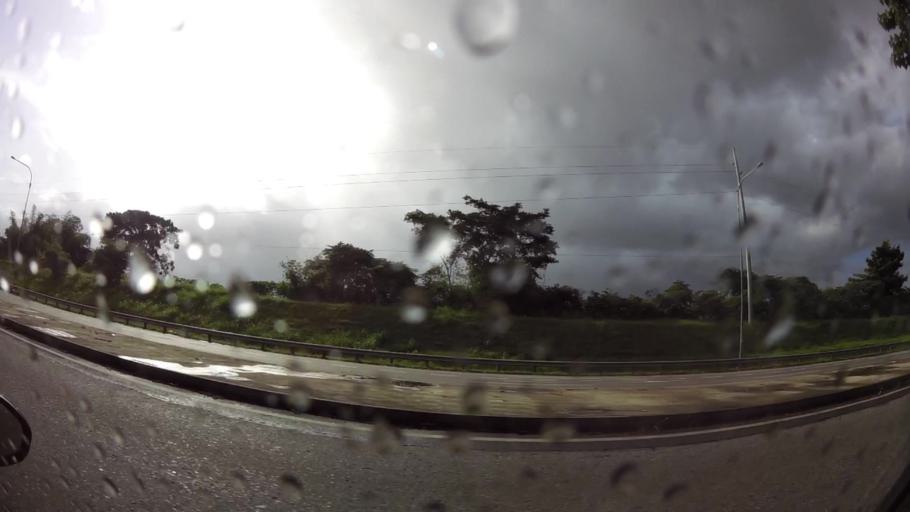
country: TT
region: Tunapuna/Piarco
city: Tunapuna
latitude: 10.6388
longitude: -61.4313
